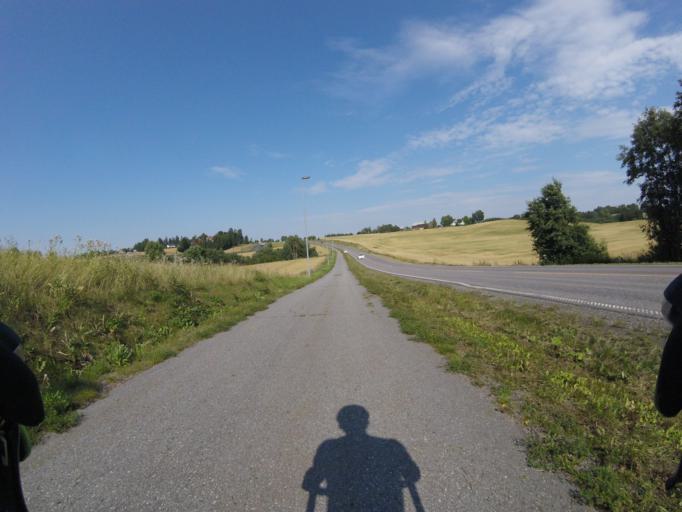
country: NO
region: Akershus
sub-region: Sorum
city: Frogner
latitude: 60.0112
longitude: 11.1099
